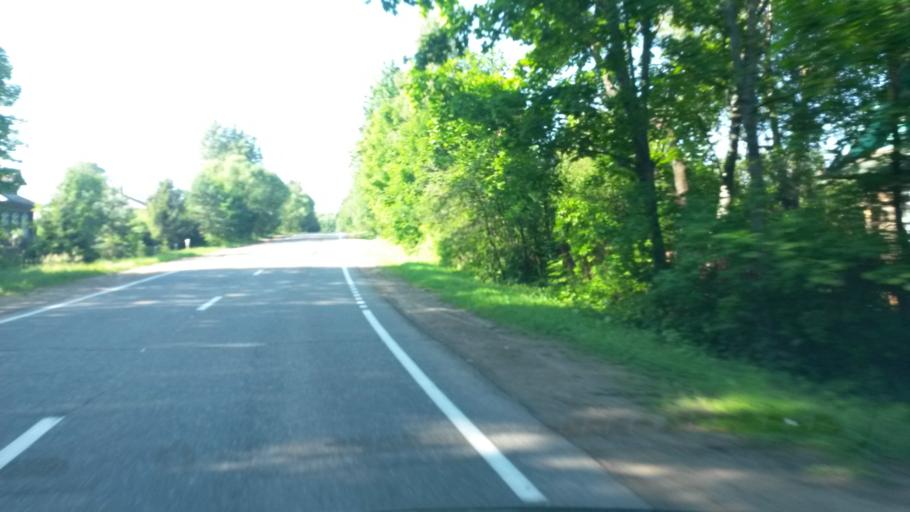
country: RU
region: Jaroslavl
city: Gavrilov-Yam
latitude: 57.2828
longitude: 39.9536
